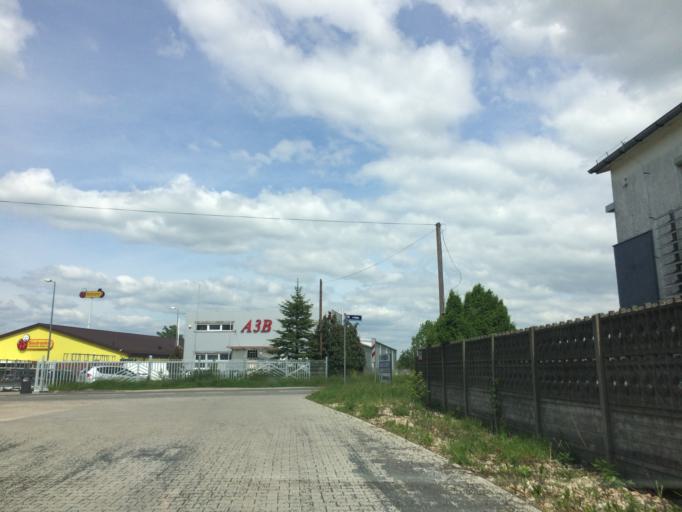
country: PL
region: Lower Silesian Voivodeship
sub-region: Powiat wroclawski
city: Dlugoleka
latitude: 51.1737
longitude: 17.1807
